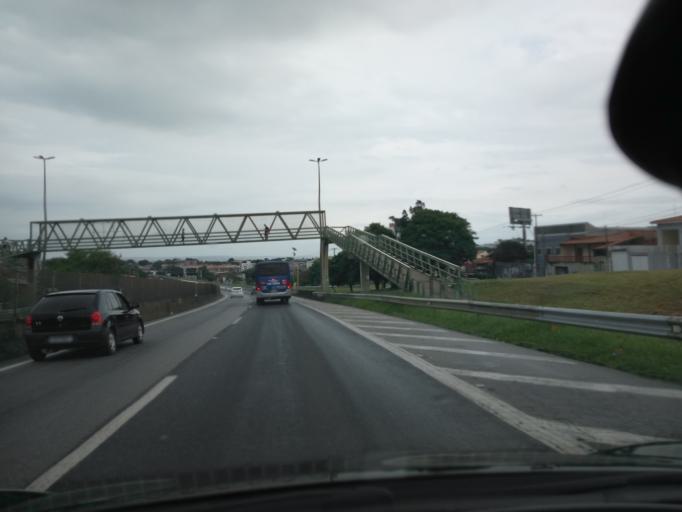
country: BR
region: Sao Paulo
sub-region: Campinas
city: Campinas
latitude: -22.9346
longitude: -47.0814
